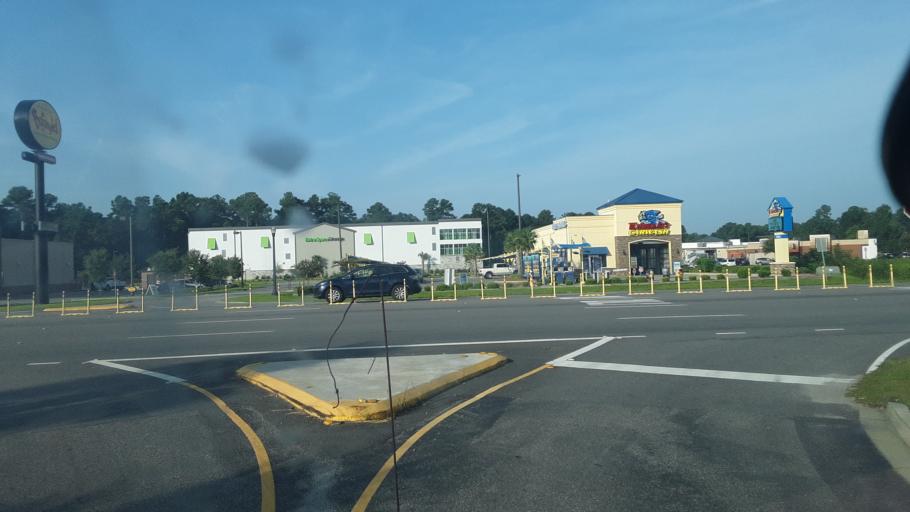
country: US
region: South Carolina
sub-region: Horry County
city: Myrtle Beach
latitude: 33.7599
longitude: -78.8582
